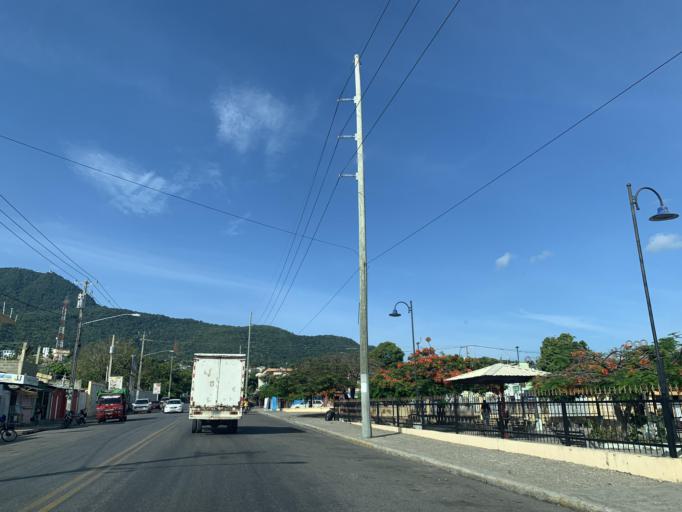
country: DO
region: Puerto Plata
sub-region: Puerto Plata
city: Puerto Plata
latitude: 19.7947
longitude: -70.7029
